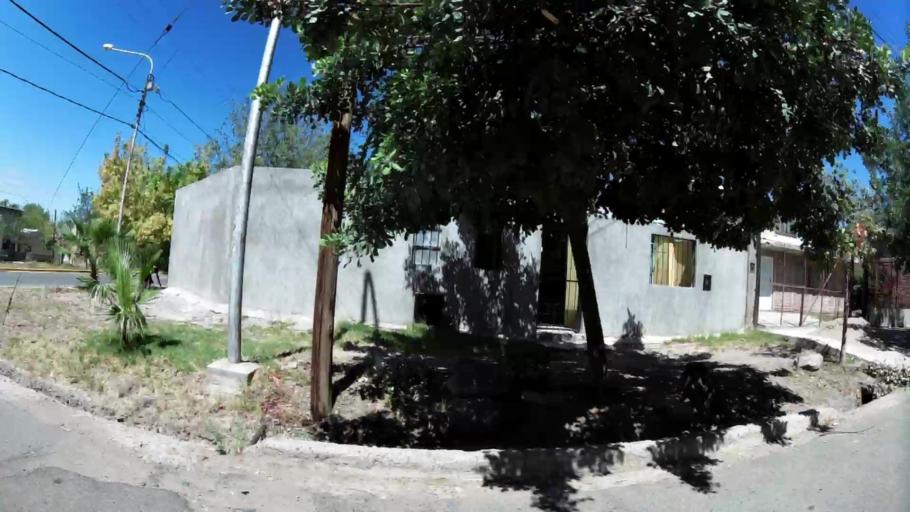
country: AR
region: Mendoza
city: Las Heras
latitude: -32.8441
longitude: -68.8735
